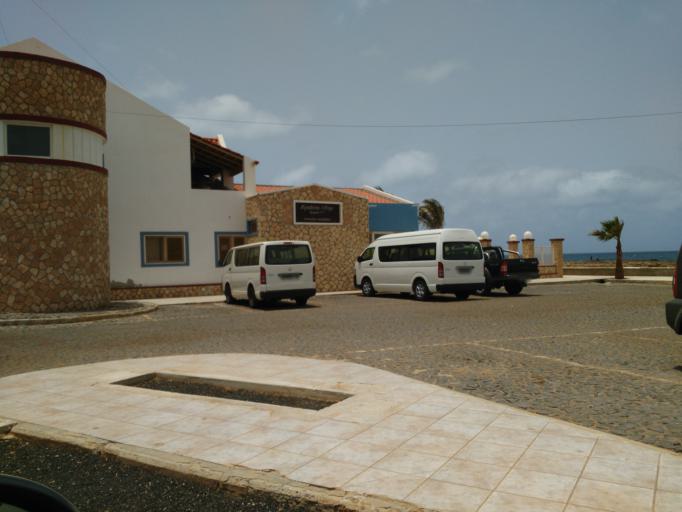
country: CV
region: Sal
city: Espargos
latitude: 16.6779
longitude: -22.9352
